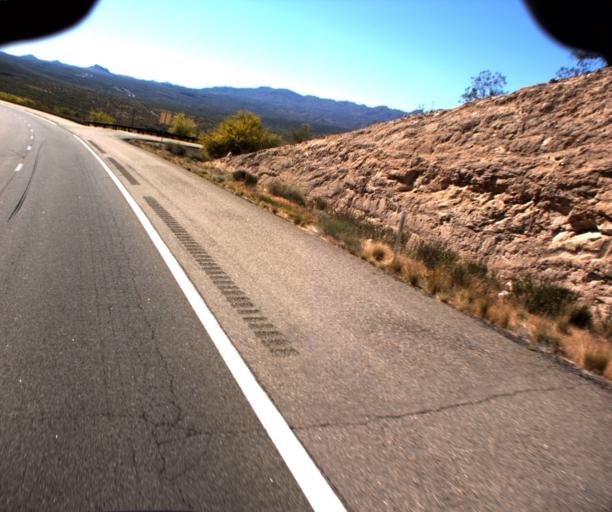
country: US
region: Arizona
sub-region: Yavapai County
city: Bagdad
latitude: 34.5475
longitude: -113.4504
